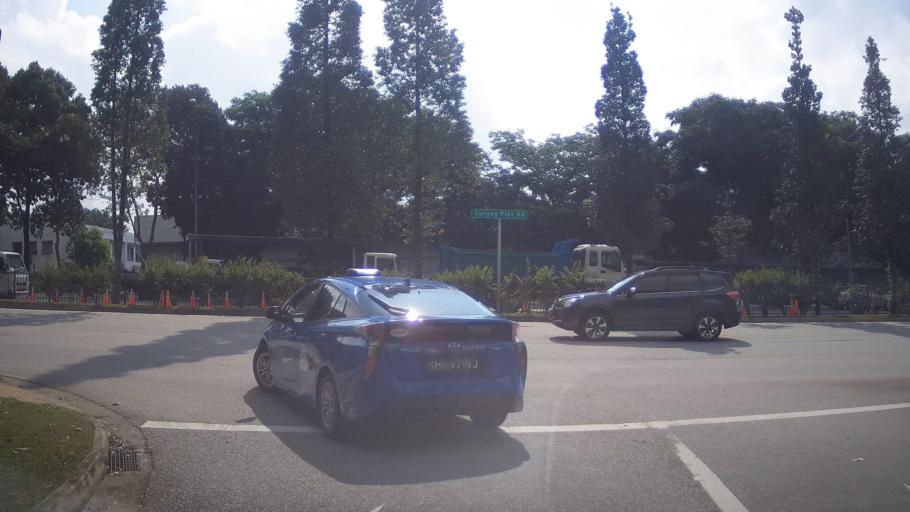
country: SG
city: Singapore
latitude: 1.3193
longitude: 103.7101
